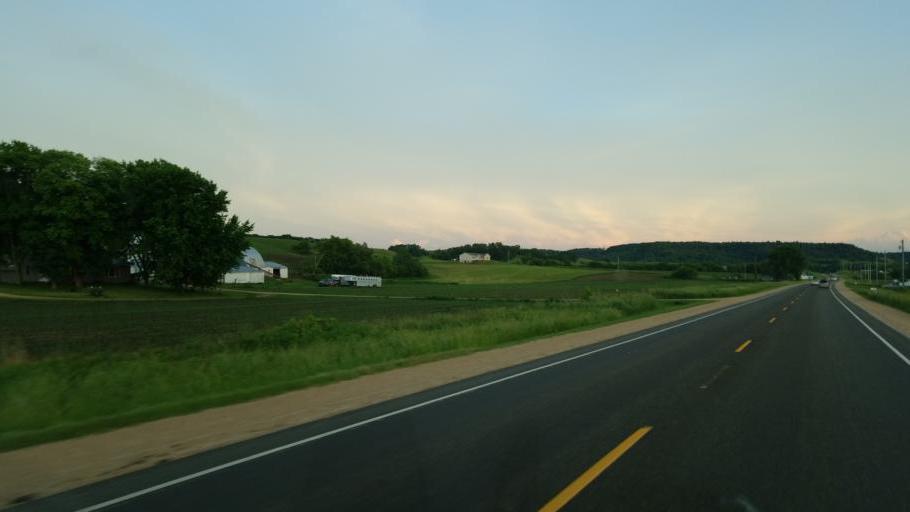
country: US
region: Wisconsin
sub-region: Monroe County
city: Tomah
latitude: 43.8465
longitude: -90.4737
